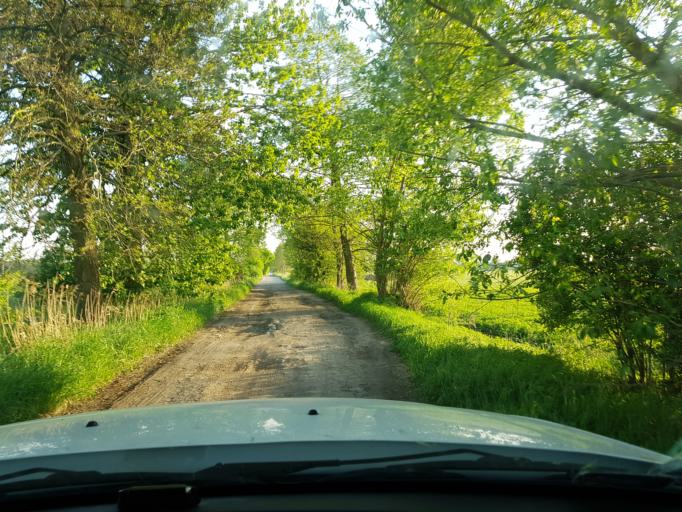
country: PL
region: West Pomeranian Voivodeship
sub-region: Powiat stargardzki
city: Kobylanka
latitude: 53.4045
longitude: 14.8905
